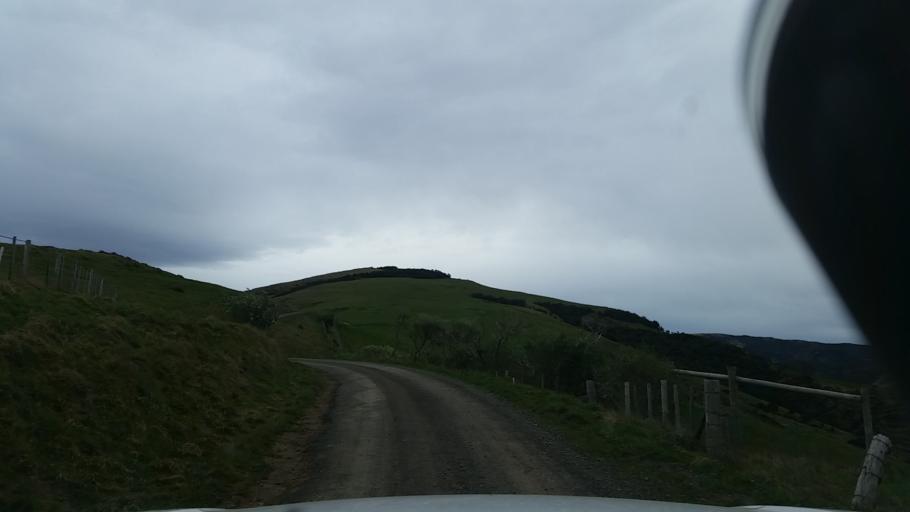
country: NZ
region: Canterbury
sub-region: Christchurch City
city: Christchurch
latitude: -43.8200
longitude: 173.0712
